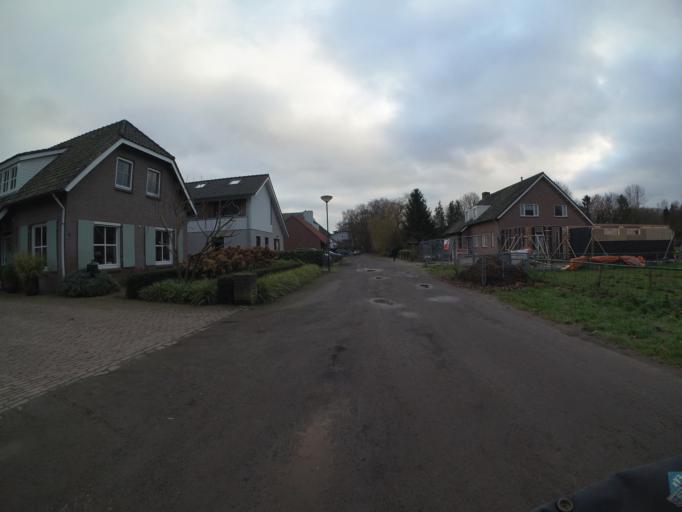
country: NL
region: North Brabant
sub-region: Gemeente Vught
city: Vught
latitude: 51.6476
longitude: 5.2787
